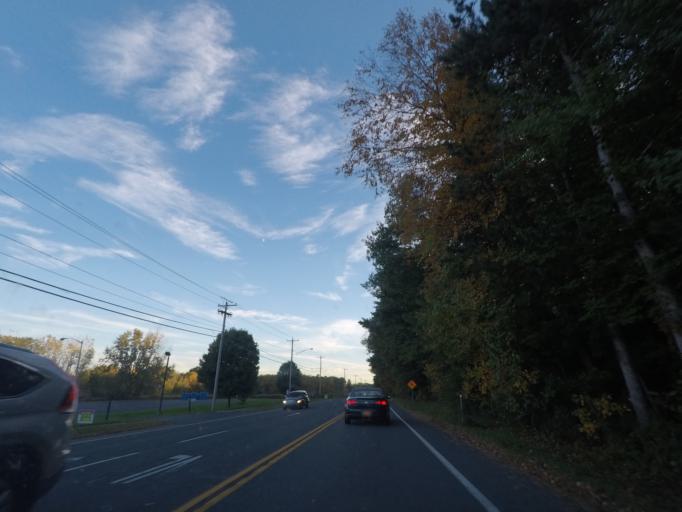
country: US
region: New York
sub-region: Albany County
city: Colonie
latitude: 42.7381
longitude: -73.8266
